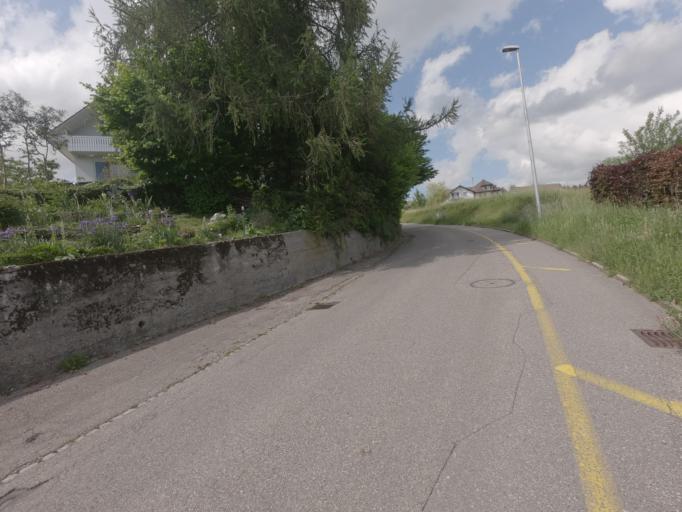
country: CH
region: Solothurn
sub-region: Bezirk Lebern
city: Riedholz
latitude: 47.2329
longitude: 7.5740
